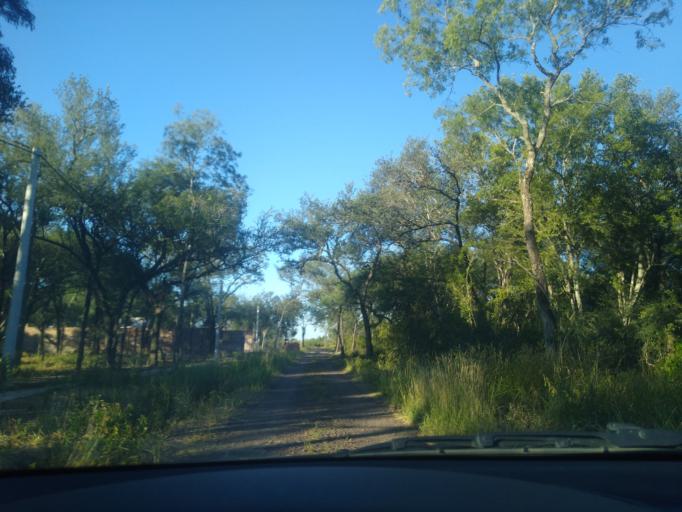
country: AR
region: Chaco
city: Resistencia
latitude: -27.4105
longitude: -58.9526
